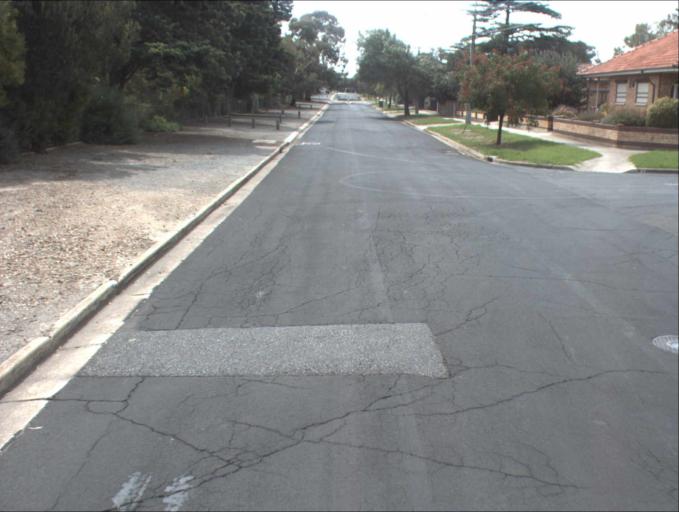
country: AU
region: South Australia
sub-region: Port Adelaide Enfield
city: Enfield
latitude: -34.8588
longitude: 138.6145
